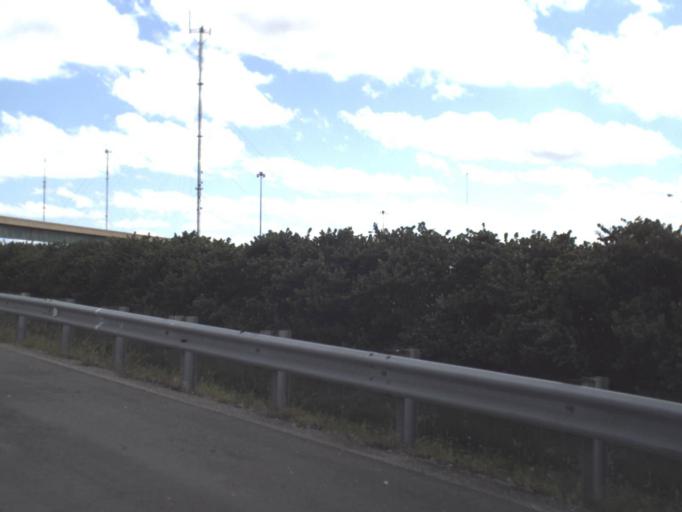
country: US
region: Florida
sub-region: Miami-Dade County
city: Lake Lucerne
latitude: 25.9727
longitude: -80.2319
